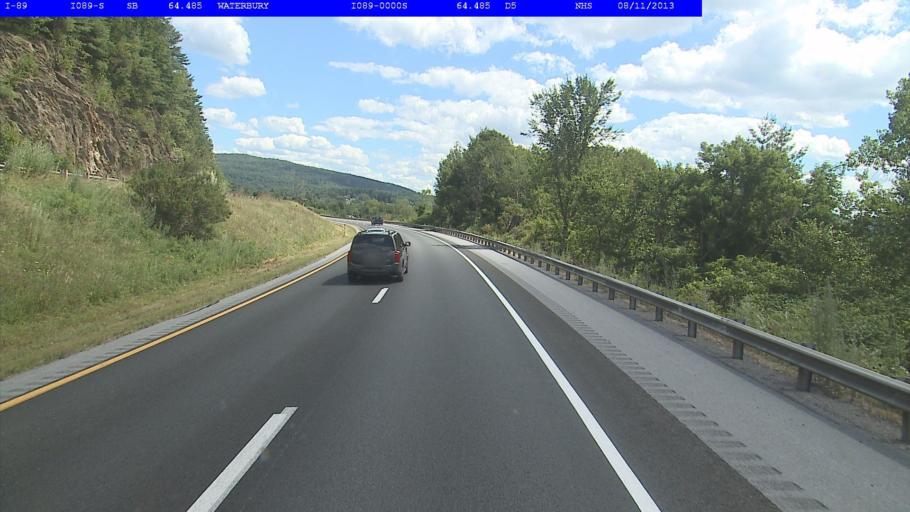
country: US
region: Vermont
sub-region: Washington County
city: Waterbury
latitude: 44.3457
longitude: -72.7665
